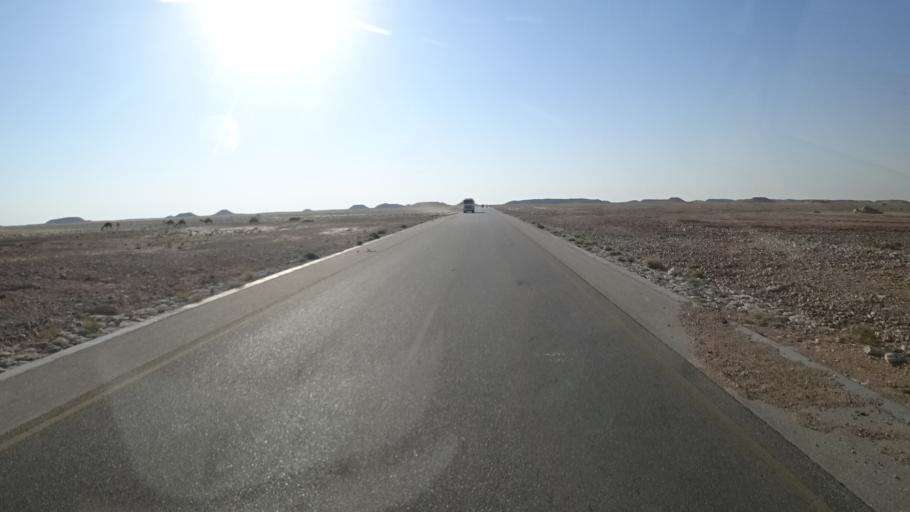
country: OM
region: Zufar
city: Salalah
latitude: 17.6416
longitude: 53.8245
